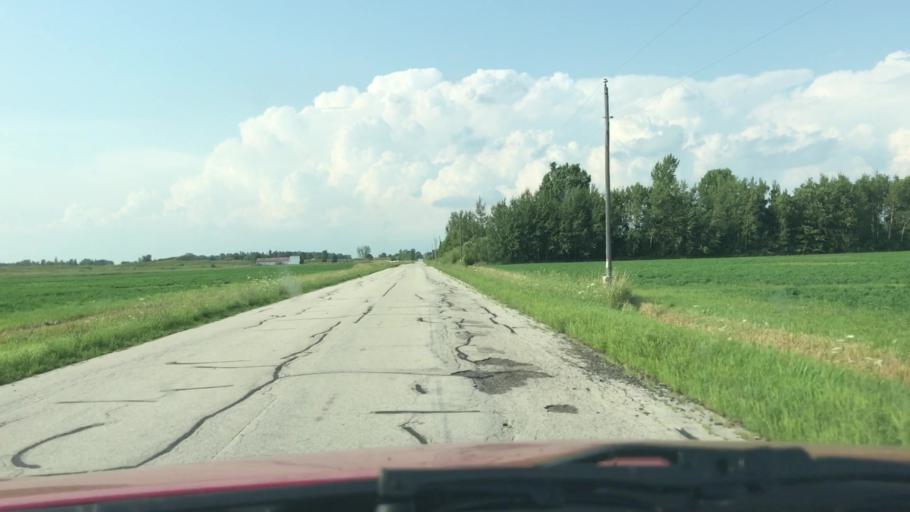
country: US
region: Wisconsin
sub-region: Brown County
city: Oneida
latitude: 44.4318
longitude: -88.1705
